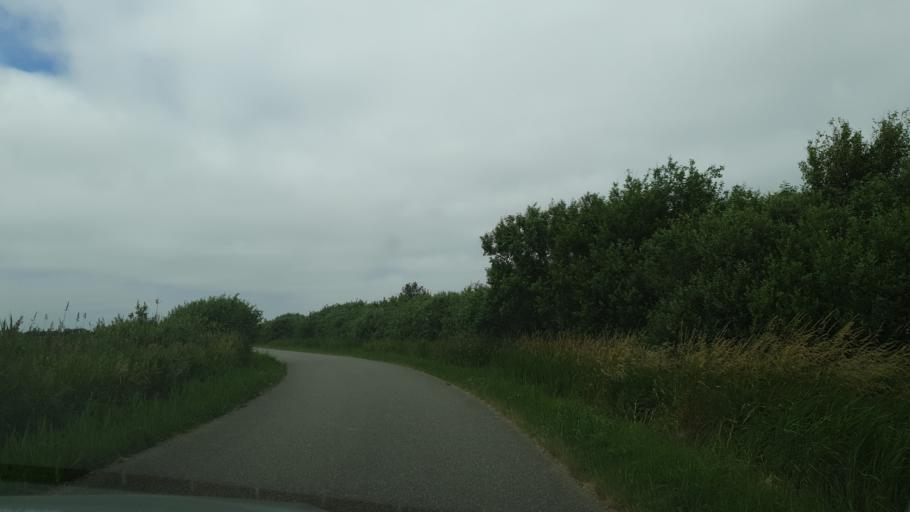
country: DK
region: Central Jutland
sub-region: Ringkobing-Skjern Kommune
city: Skjern
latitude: 55.9203
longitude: 8.4063
